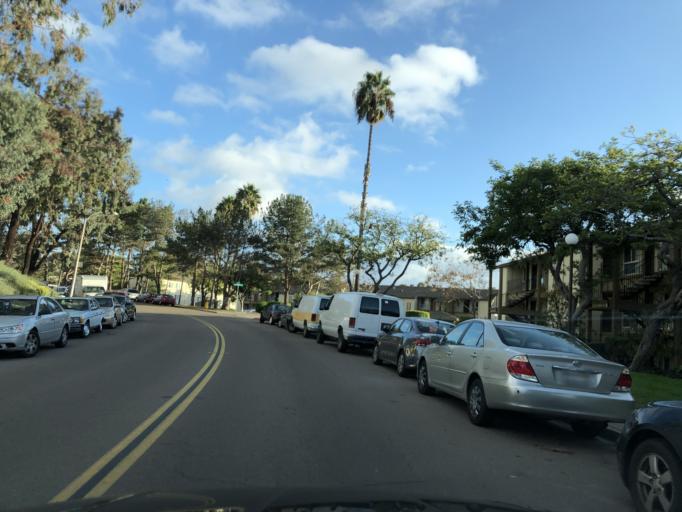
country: US
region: California
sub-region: San Diego County
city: La Jolla
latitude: 32.8175
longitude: -117.1773
